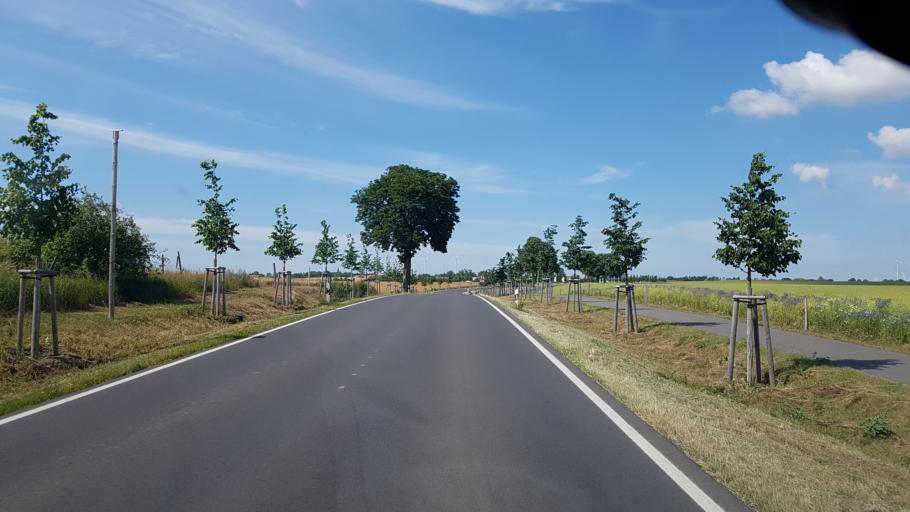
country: DE
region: Brandenburg
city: Gramzow
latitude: 53.2190
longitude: 13.9916
